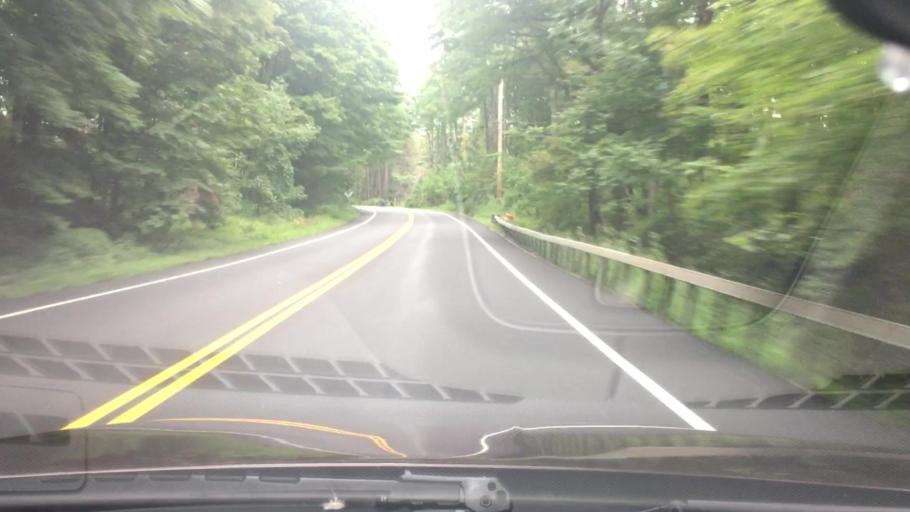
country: US
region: New York
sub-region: Dutchess County
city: Dover Plains
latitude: 41.8410
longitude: -73.5769
